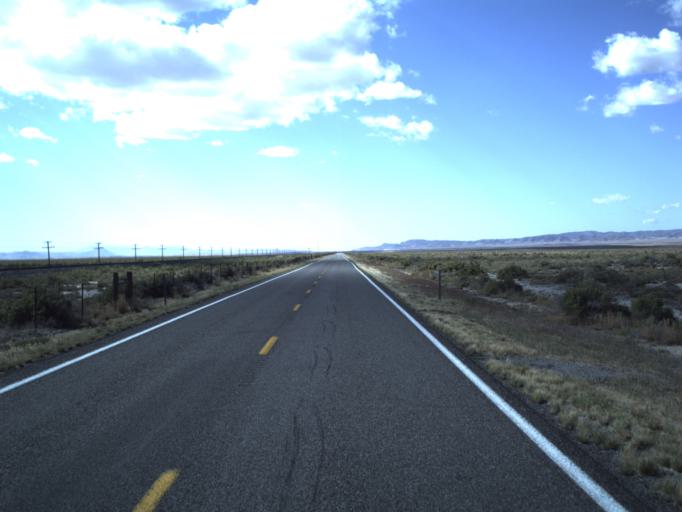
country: US
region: Utah
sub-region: Millard County
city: Delta
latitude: 39.0892
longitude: -112.7520
